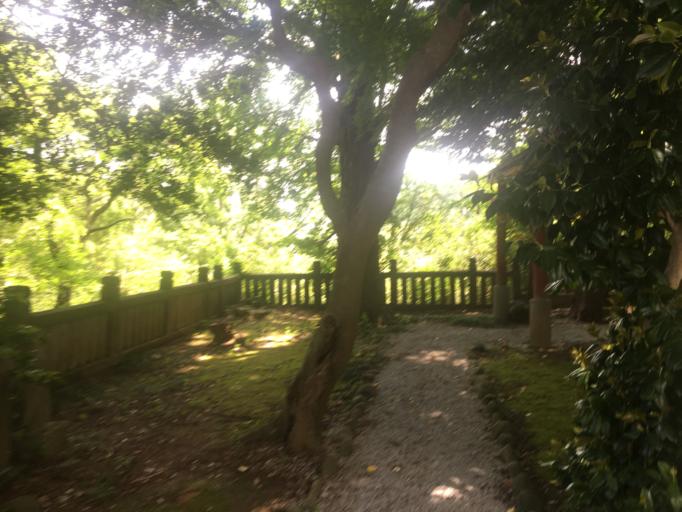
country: JP
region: Saitama
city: Morohongo
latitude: 35.9622
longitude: 139.2942
